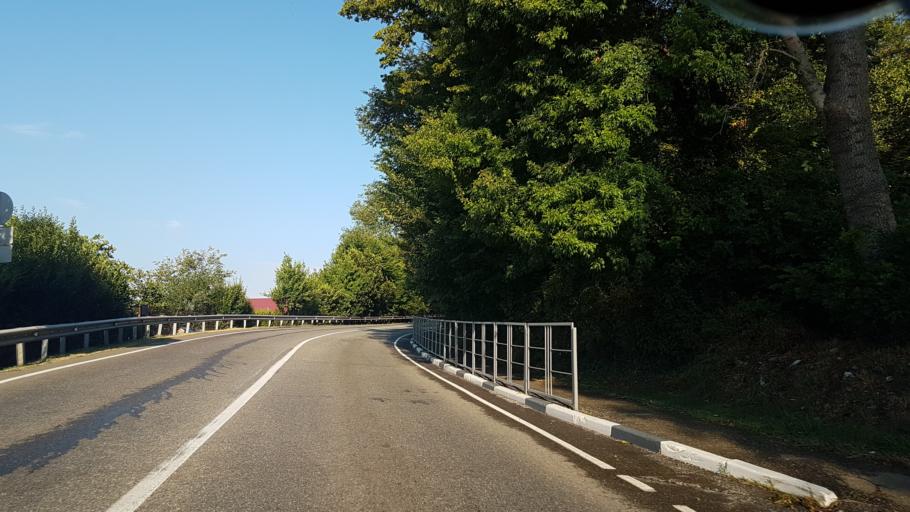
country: RU
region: Krasnodarskiy
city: Vardane
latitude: 43.7685
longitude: 39.4967
